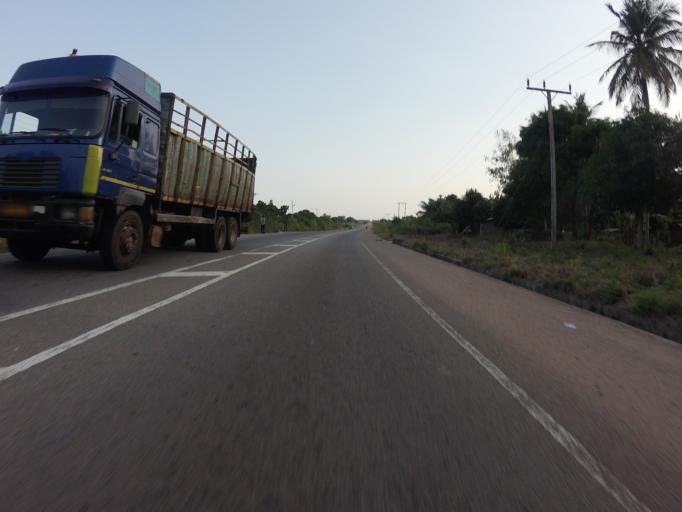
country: GH
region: Volta
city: Anloga
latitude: 6.0339
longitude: 0.6045
